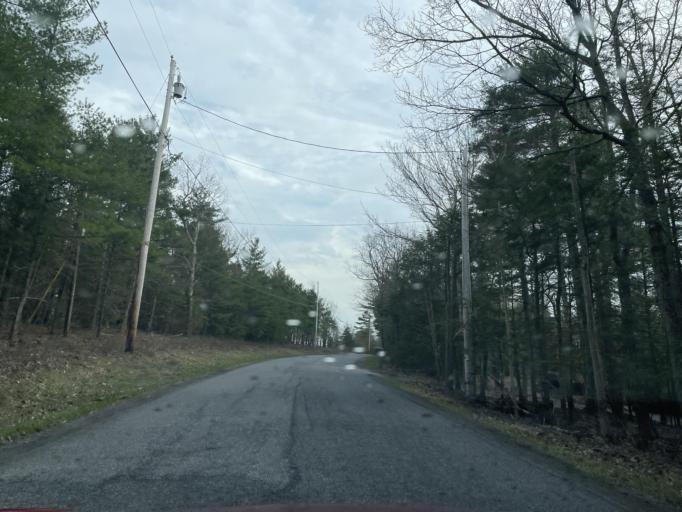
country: US
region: New York
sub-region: Ulster County
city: Manorville
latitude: 42.1321
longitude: -74.0402
